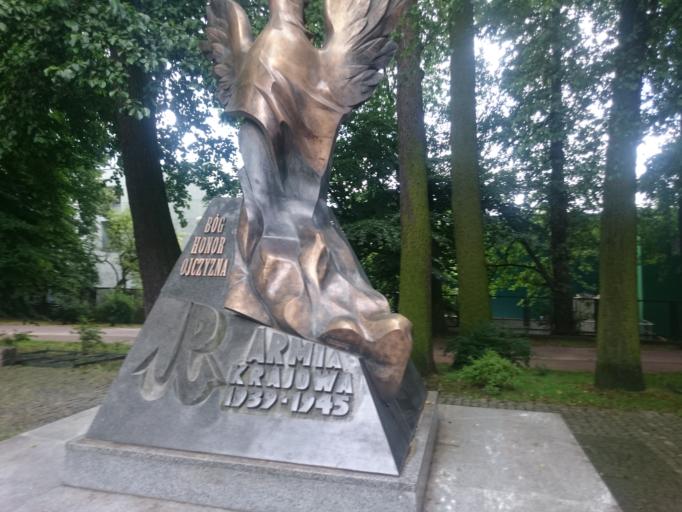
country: PL
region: Pomeranian Voivodeship
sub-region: Sopot
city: Sopot
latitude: 54.4426
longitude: 18.5567
